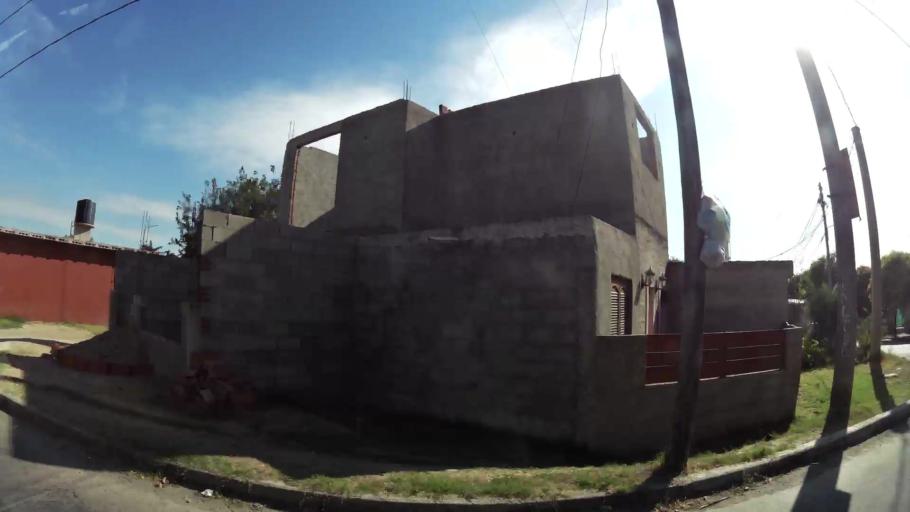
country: AR
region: Cordoba
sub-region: Departamento de Capital
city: Cordoba
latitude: -31.4412
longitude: -64.2133
